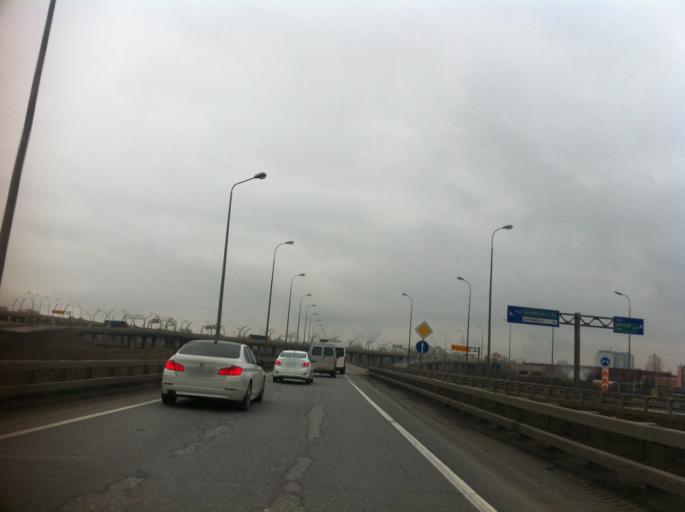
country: RU
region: St.-Petersburg
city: Dachnoye
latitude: 59.8325
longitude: 30.2849
